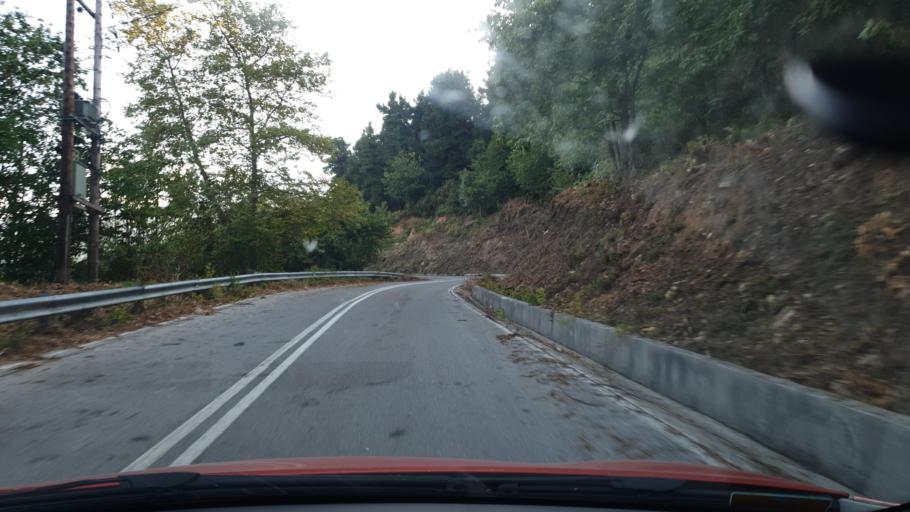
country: GR
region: Central Greece
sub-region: Nomos Evvoias
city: Kymi
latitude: 38.6341
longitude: 23.9351
